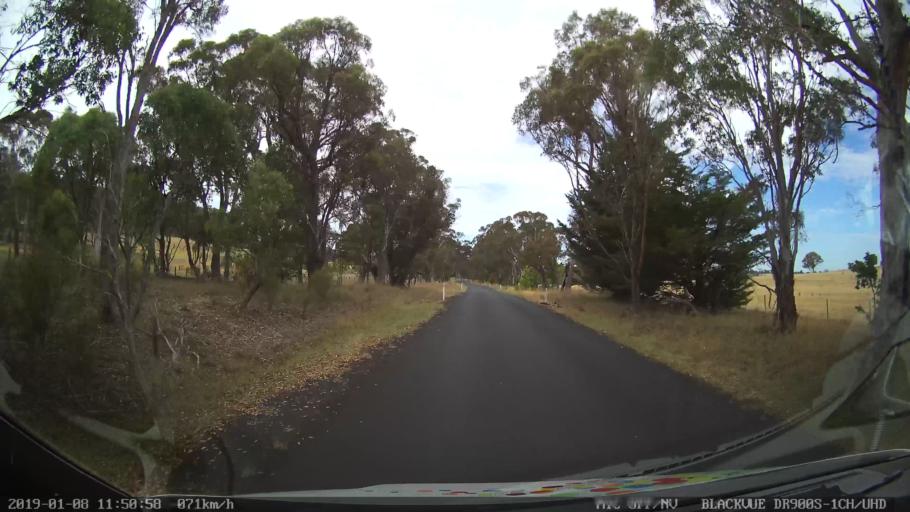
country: AU
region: New South Wales
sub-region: Armidale Dumaresq
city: Armidale
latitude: -30.3882
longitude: 151.5581
